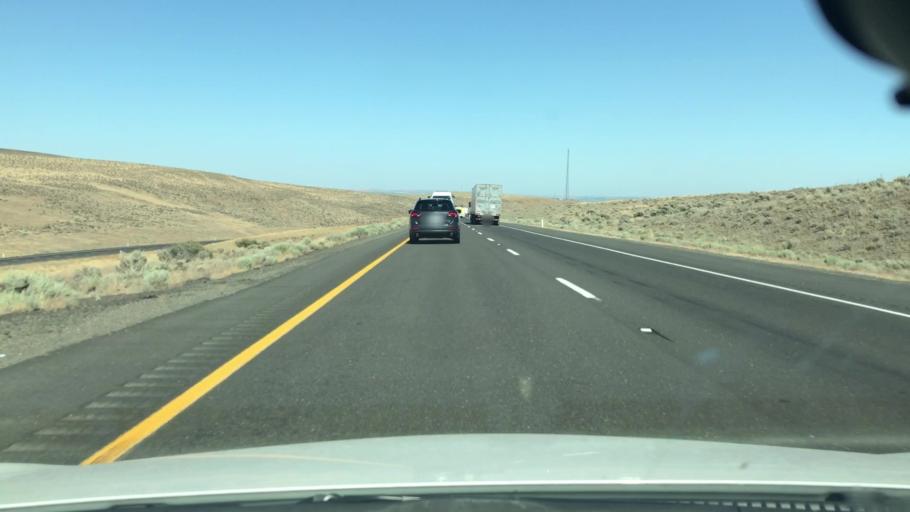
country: US
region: Washington
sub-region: Grant County
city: Mattawa
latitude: 46.9450
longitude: -120.0967
